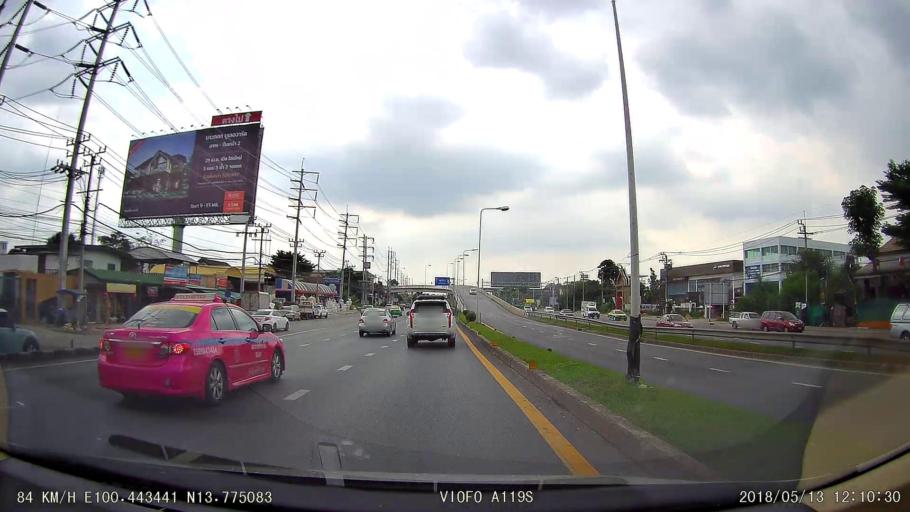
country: TH
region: Bangkok
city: Taling Chan
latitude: 13.7754
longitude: 100.4434
